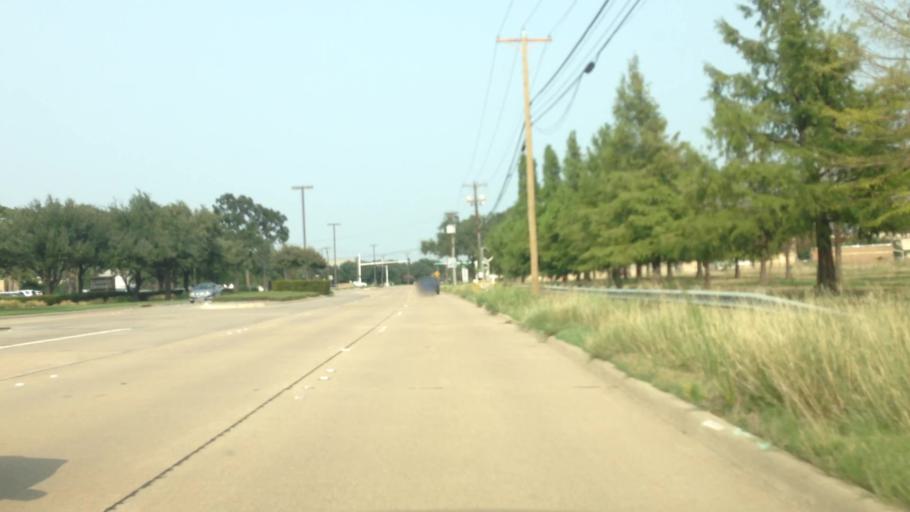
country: US
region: Texas
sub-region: Dallas County
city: Farmers Branch
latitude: 32.9214
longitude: -96.9151
